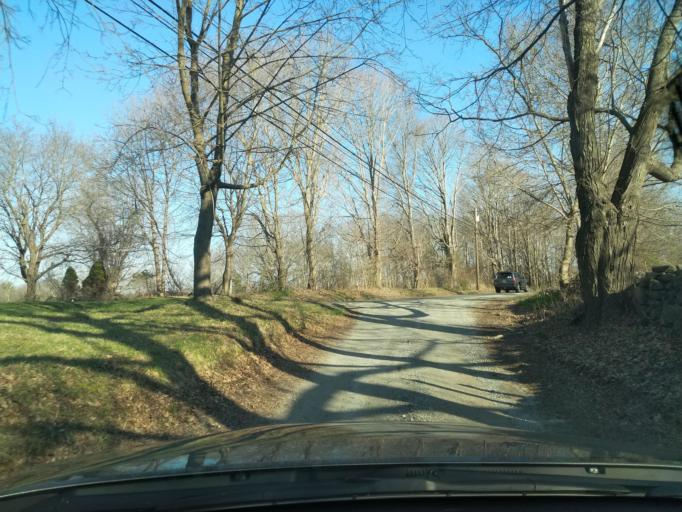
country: US
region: Connecticut
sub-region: Fairfield County
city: Newtown
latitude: 41.3650
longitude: -73.2840
